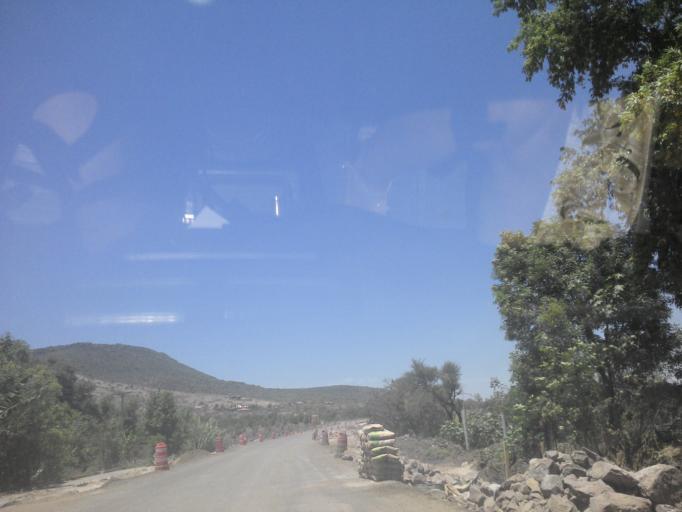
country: MX
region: Guanajuato
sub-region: San Francisco del Rincon
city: San Ignacio de Hidalgo
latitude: 20.9295
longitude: -101.9176
